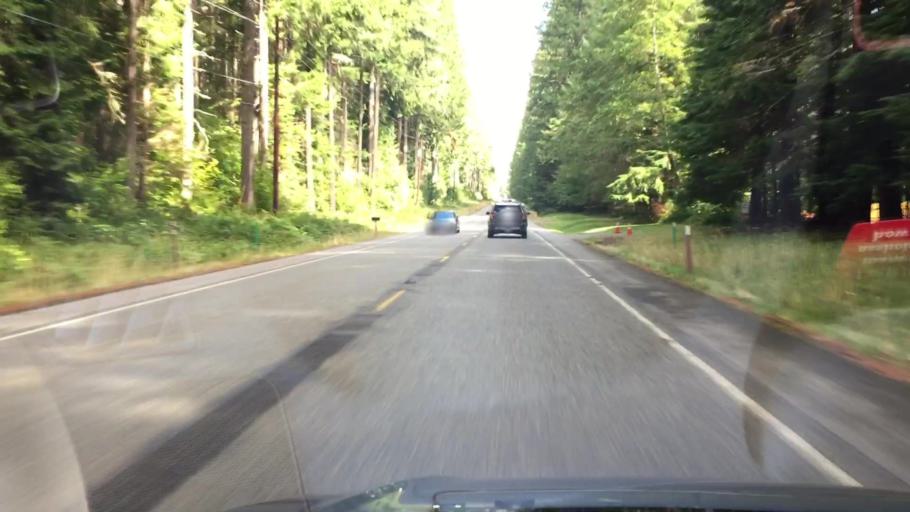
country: US
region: Washington
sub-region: Pierce County
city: Eatonville
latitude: 46.7562
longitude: -122.0833
